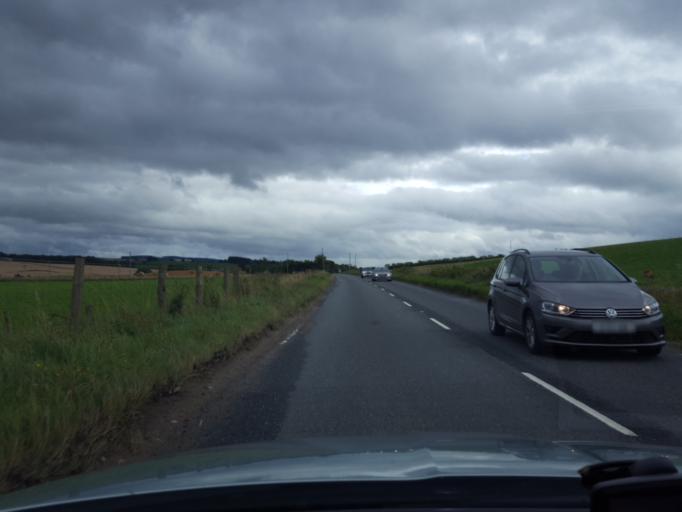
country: GB
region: Scotland
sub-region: Aberdeenshire
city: Kemnay
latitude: 57.1749
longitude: -2.4281
